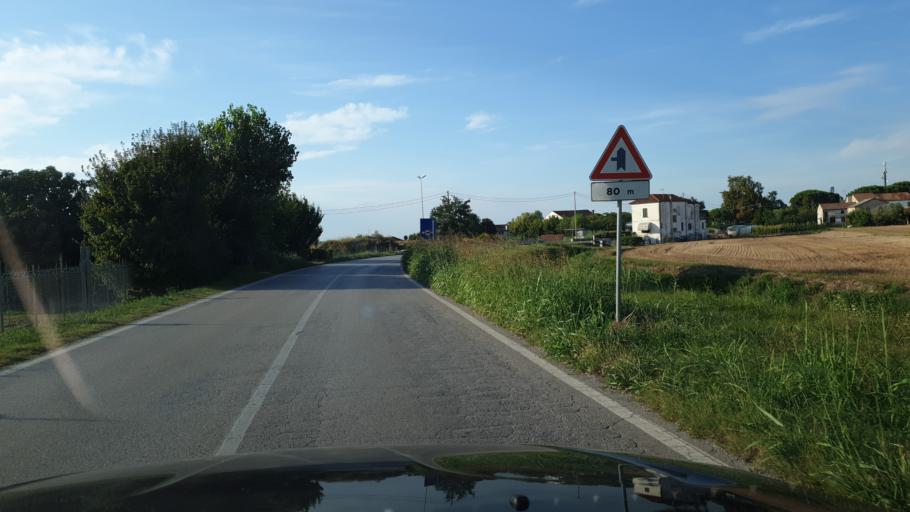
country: IT
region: Veneto
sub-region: Provincia di Rovigo
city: Fiesso Umbertiano
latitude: 44.9679
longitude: 11.6108
